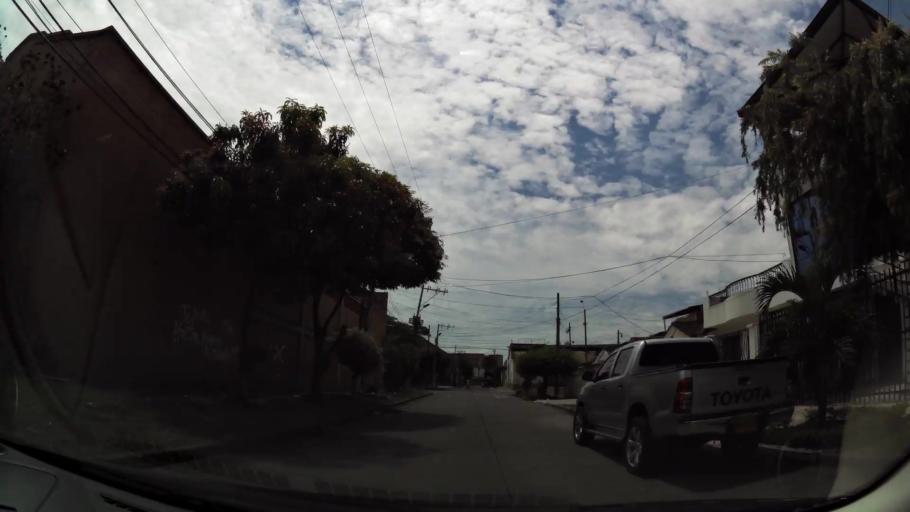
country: CO
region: Valle del Cauca
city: Cali
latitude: 3.4499
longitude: -76.5140
